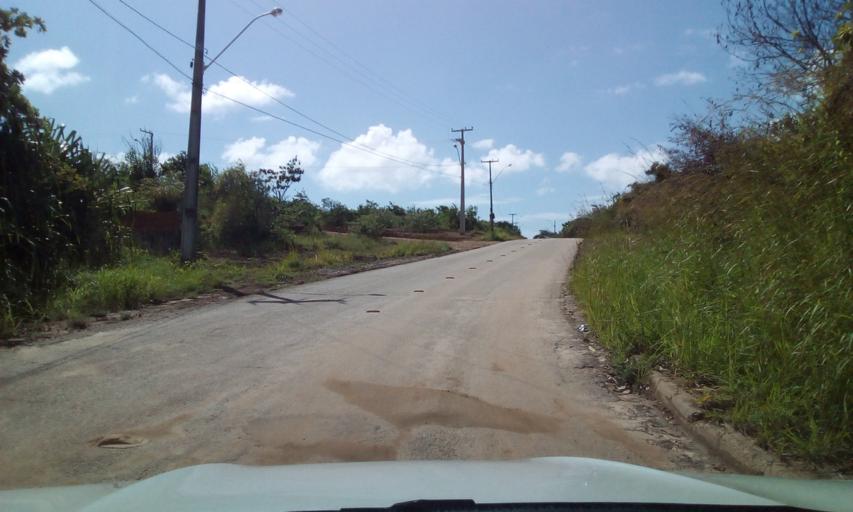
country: BR
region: Paraiba
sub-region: Conde
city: Conde
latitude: -7.2172
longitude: -34.8096
